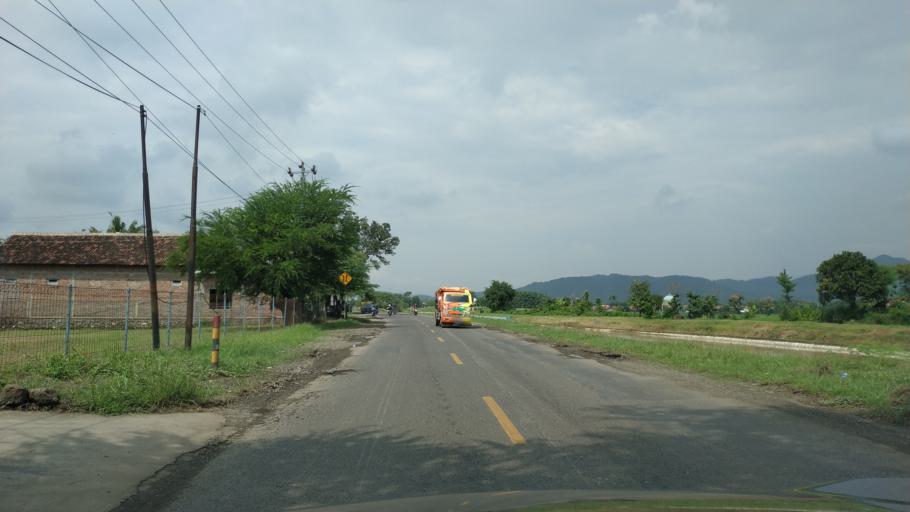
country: ID
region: Central Java
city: Margasari
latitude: -7.0871
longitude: 108.9839
